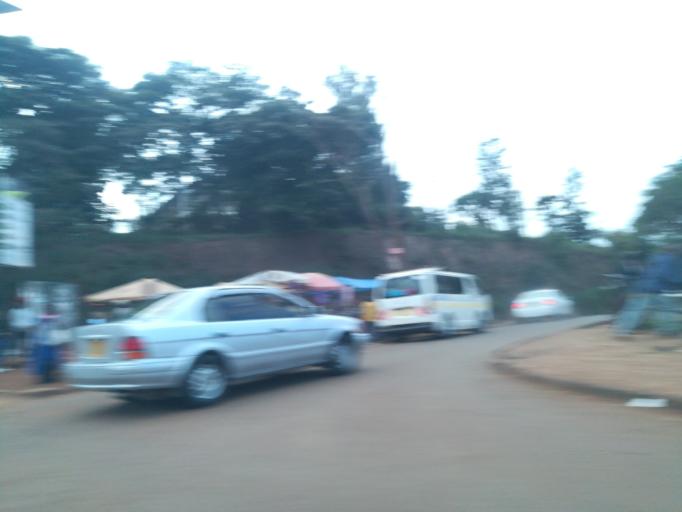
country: KE
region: Nairobi Area
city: Thika
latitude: -1.0241
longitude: 37.0664
